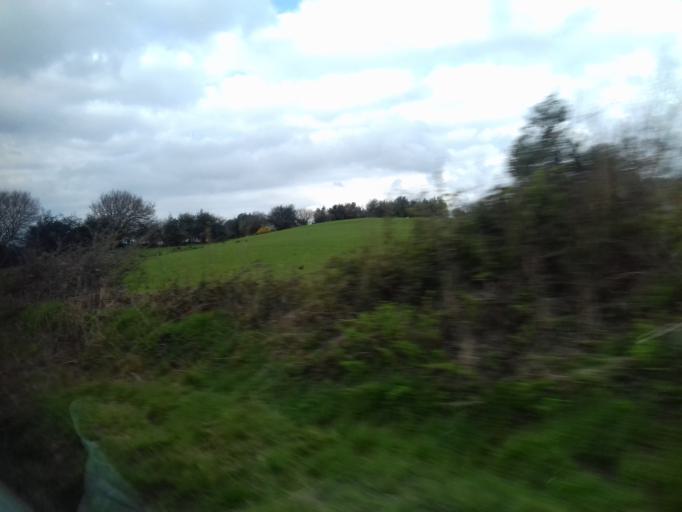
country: IE
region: Leinster
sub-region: An Iarmhi
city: An Muileann gCearr
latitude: 53.5817
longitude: -7.3778
